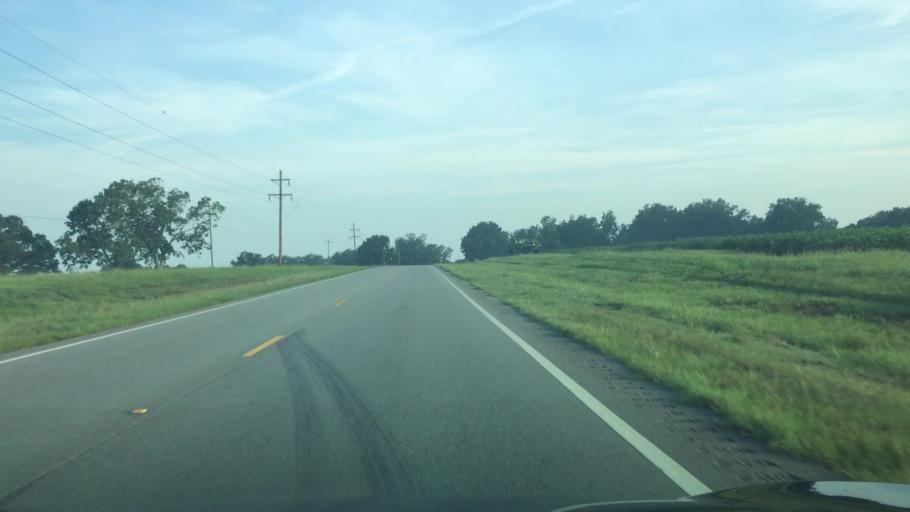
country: US
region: Alabama
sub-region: Covington County
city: Florala
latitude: 31.0457
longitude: -86.3844
